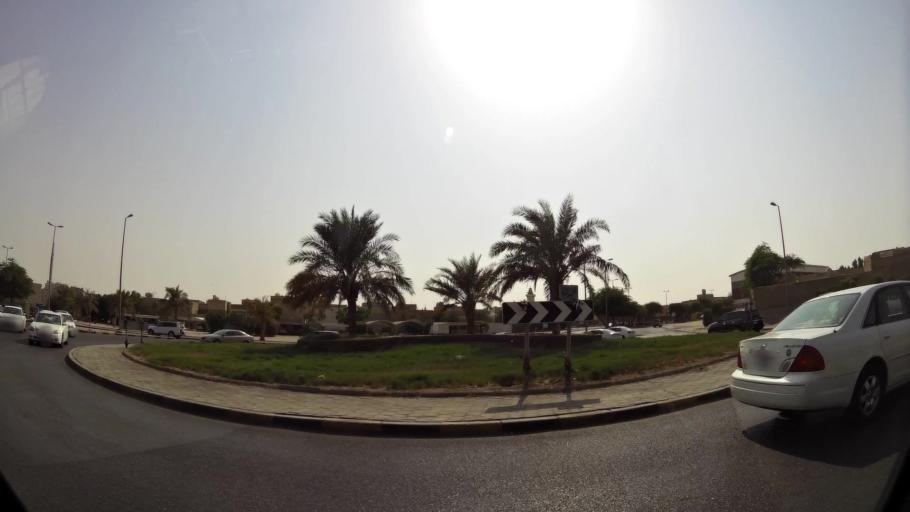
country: KW
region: Muhafazat al Jahra'
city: Al Jahra'
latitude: 29.3440
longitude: 47.6656
